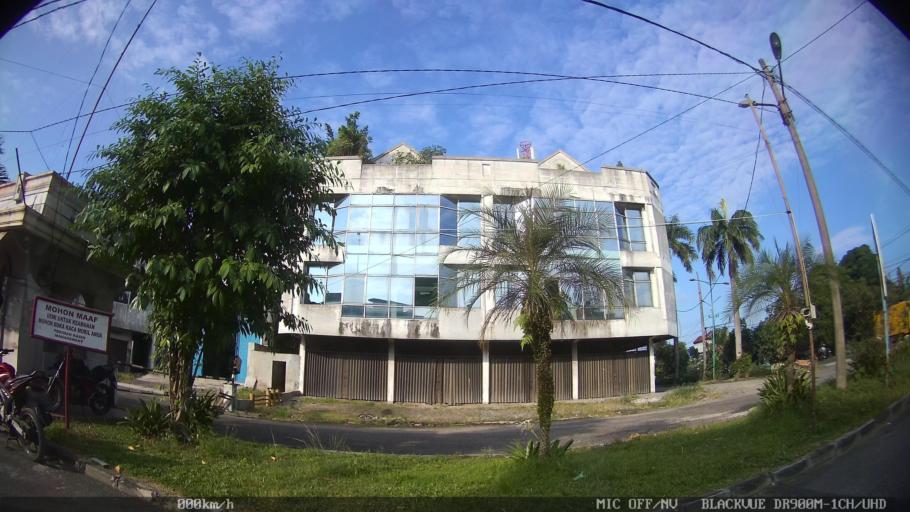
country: ID
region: North Sumatra
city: Medan
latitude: 3.6190
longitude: 98.6555
